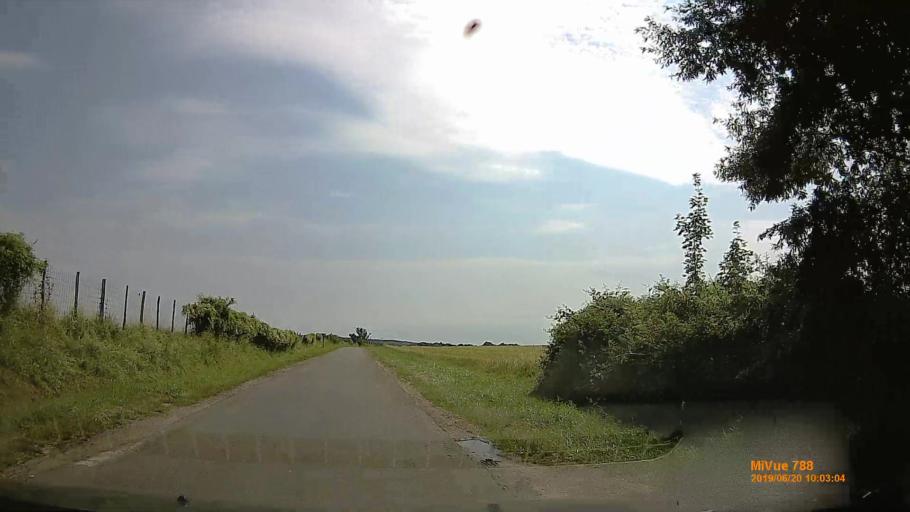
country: HU
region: Baranya
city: Mecseknadasd
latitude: 46.1954
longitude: 18.4551
